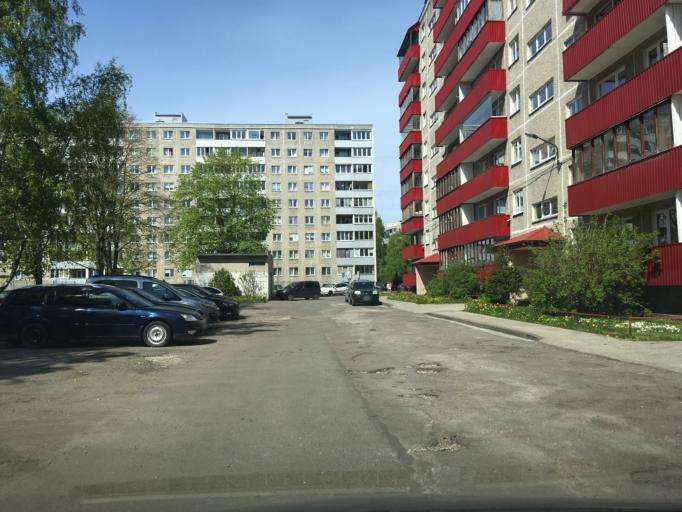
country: EE
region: Harju
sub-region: Tallinna linn
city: Kose
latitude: 59.4342
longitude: 24.8237
